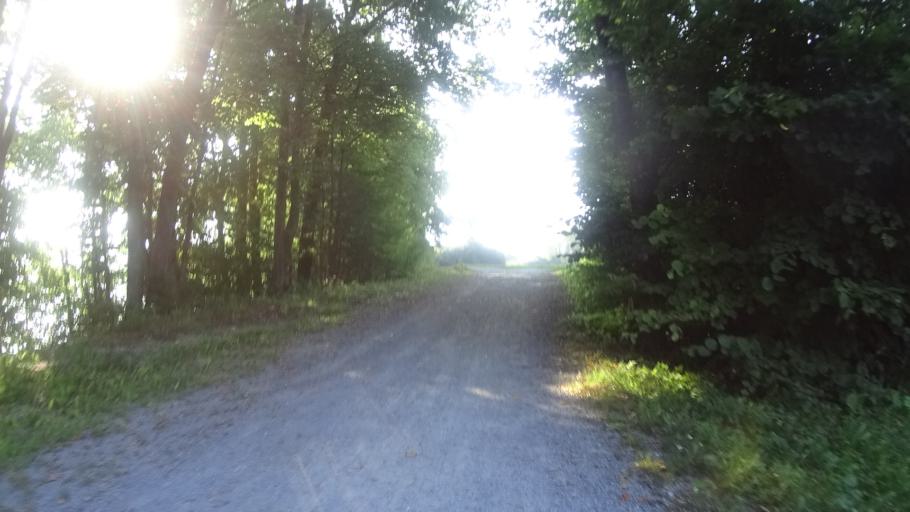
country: AT
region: Carinthia
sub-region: Politischer Bezirk Klagenfurt Land
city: Ludmannsdorf
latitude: 46.5321
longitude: 14.1379
